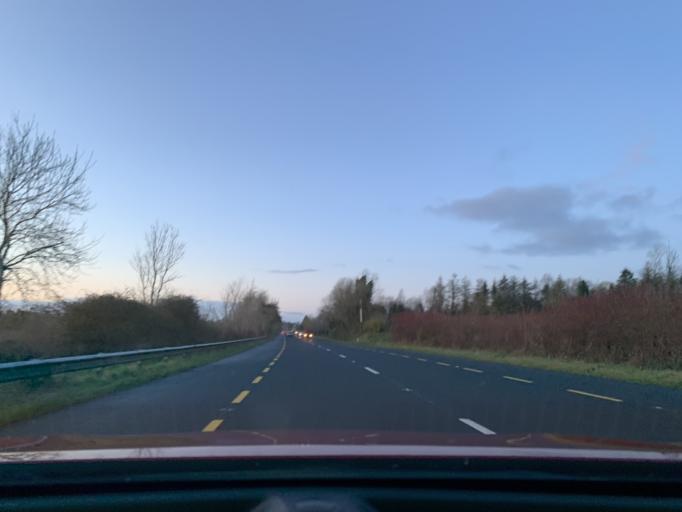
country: IE
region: Connaught
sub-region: County Leitrim
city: Carrick-on-Shannon
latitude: 53.9072
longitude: -7.9620
